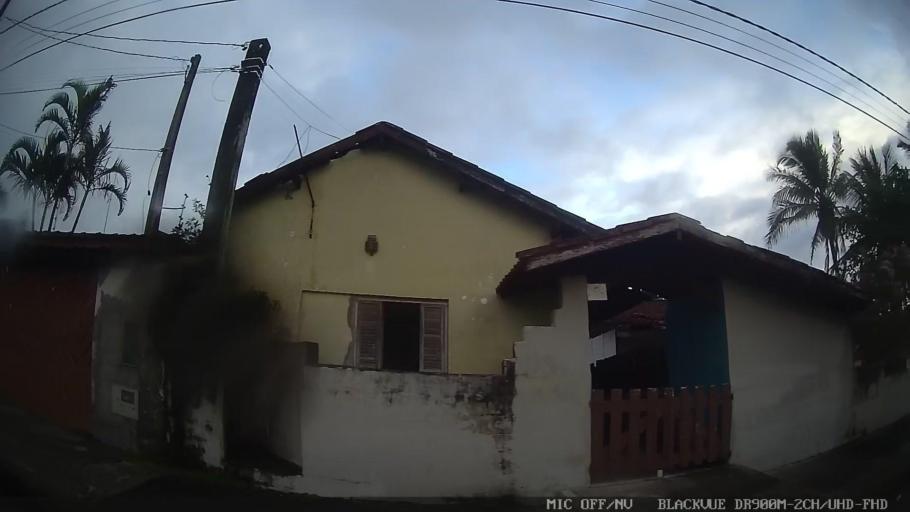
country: BR
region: Sao Paulo
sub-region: Itanhaem
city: Itanhaem
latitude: -24.2026
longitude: -46.8315
